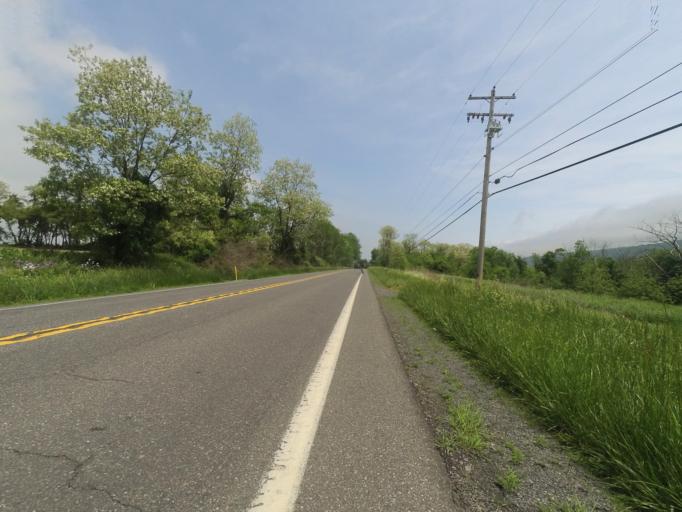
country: US
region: Pennsylvania
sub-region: Centre County
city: Pine Grove Mills
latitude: 40.7060
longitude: -77.9736
